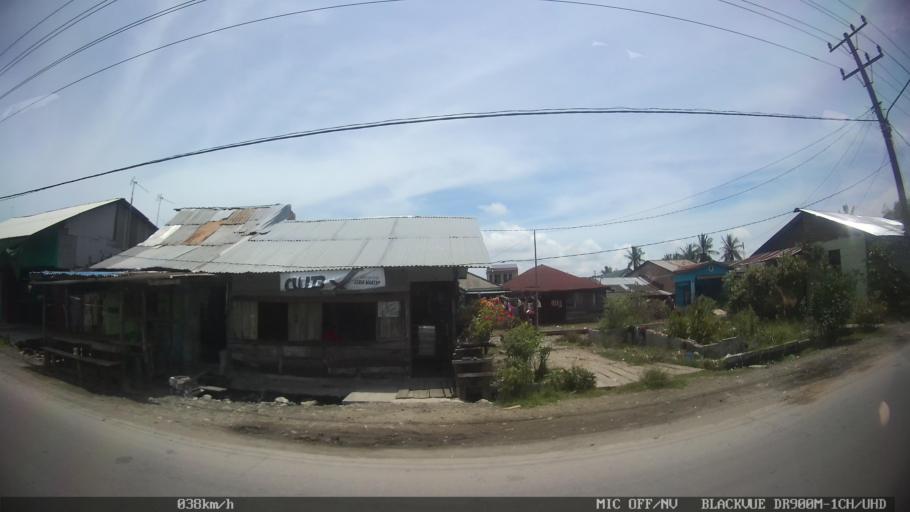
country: ID
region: North Sumatra
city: Belawan
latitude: 3.7625
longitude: 98.6818
